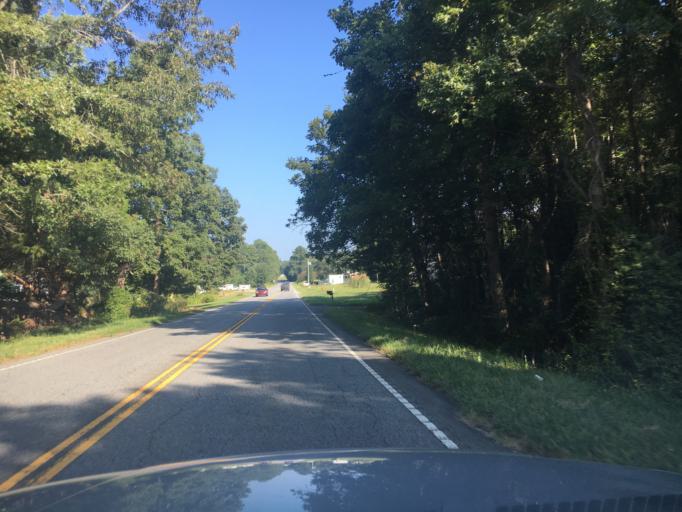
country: US
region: South Carolina
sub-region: Anderson County
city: Honea Path
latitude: 34.4636
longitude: -82.4198
